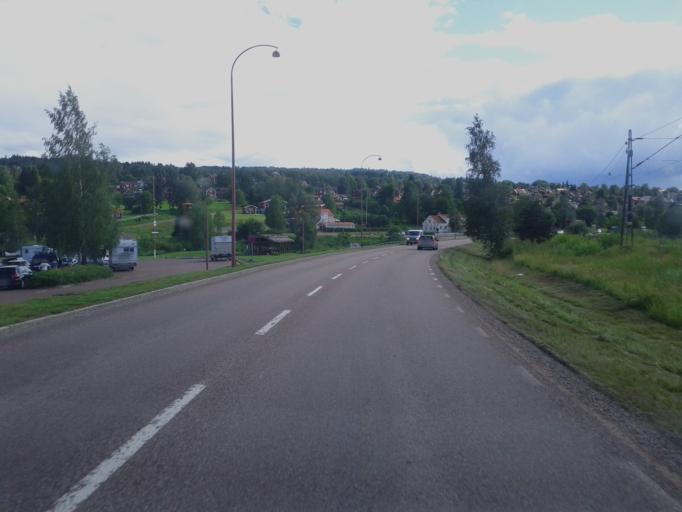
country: SE
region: Dalarna
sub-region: Rattviks Kommun
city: Raettvik
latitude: 60.8823
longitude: 15.1185
